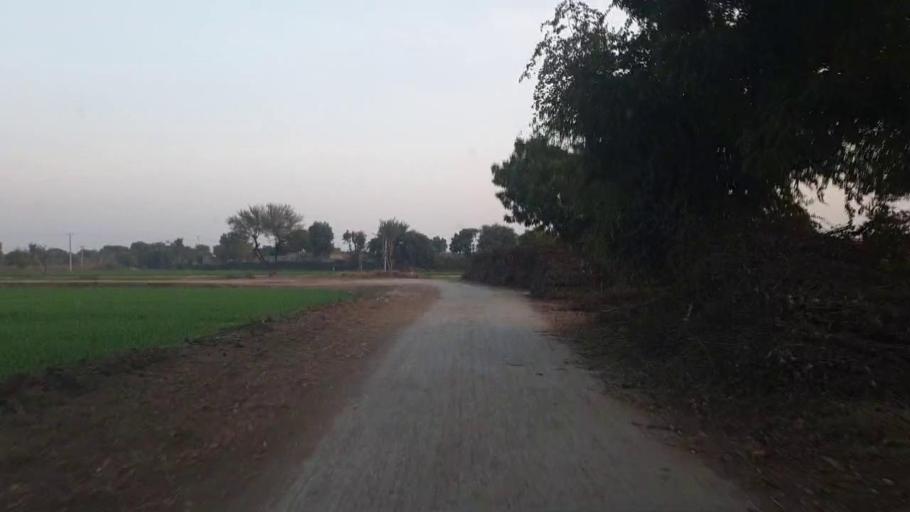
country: PK
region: Sindh
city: Bhit Shah
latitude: 25.8435
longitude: 68.5258
